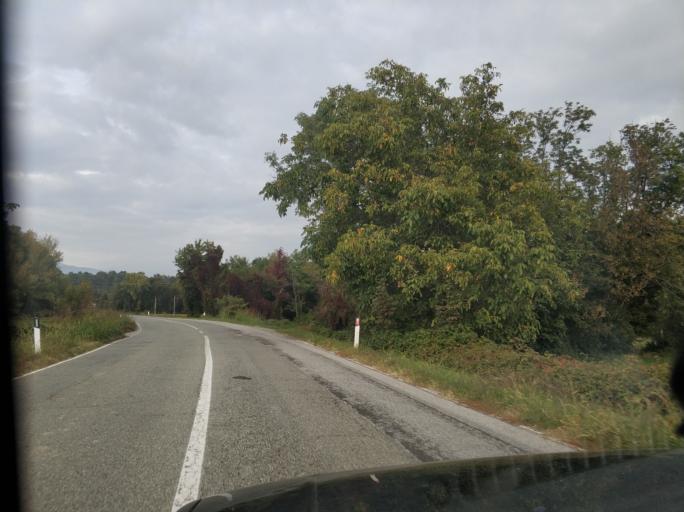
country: IT
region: Piedmont
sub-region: Provincia di Torino
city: Grosso
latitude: 45.2548
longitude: 7.5622
